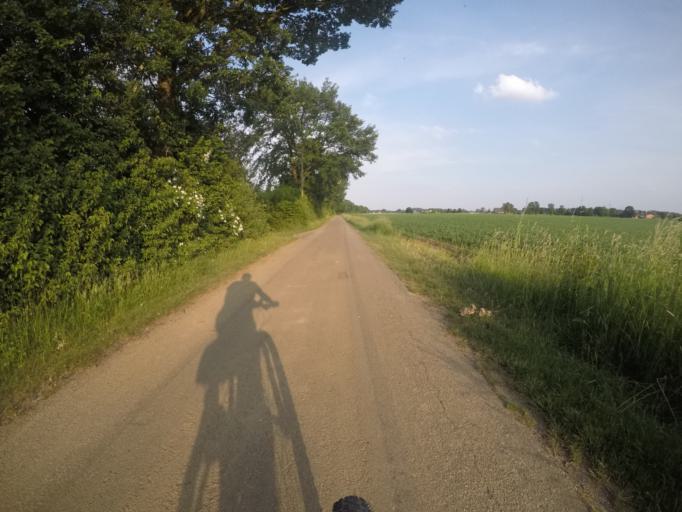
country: DE
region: North Rhine-Westphalia
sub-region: Regierungsbezirk Munster
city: Isselburg
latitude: 51.8209
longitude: 6.4891
